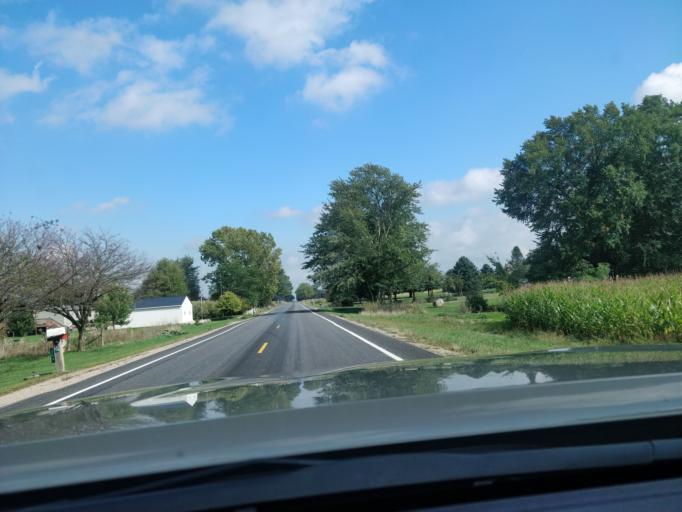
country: US
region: Michigan
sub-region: Ionia County
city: Ionia
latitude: 42.8861
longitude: -85.0904
